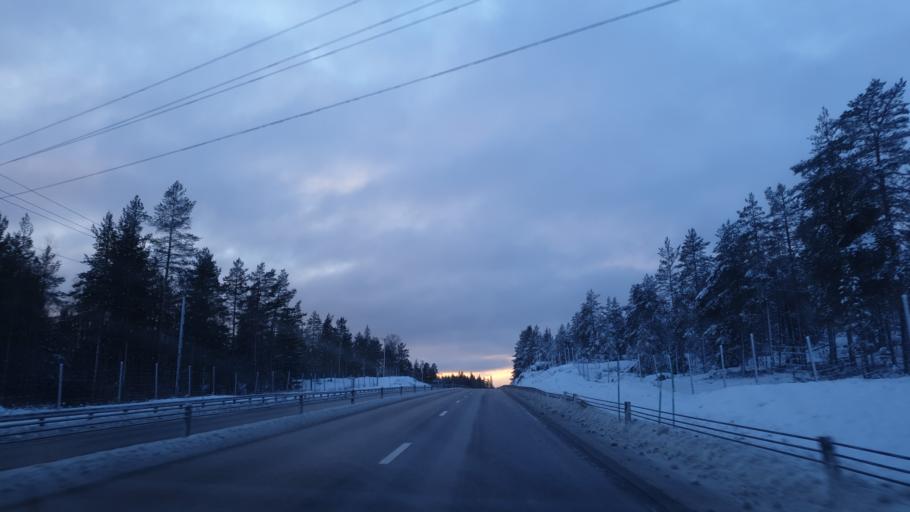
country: SE
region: Vaesterbotten
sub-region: Nordmalings Kommun
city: Nordmaling
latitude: 63.4924
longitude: 19.3165
